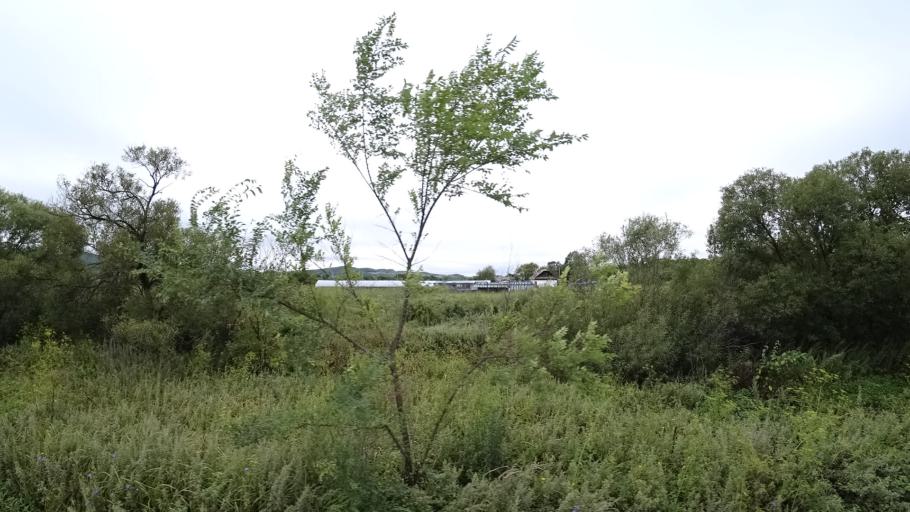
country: RU
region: Primorskiy
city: Monastyrishche
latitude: 44.1845
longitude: 132.4829
